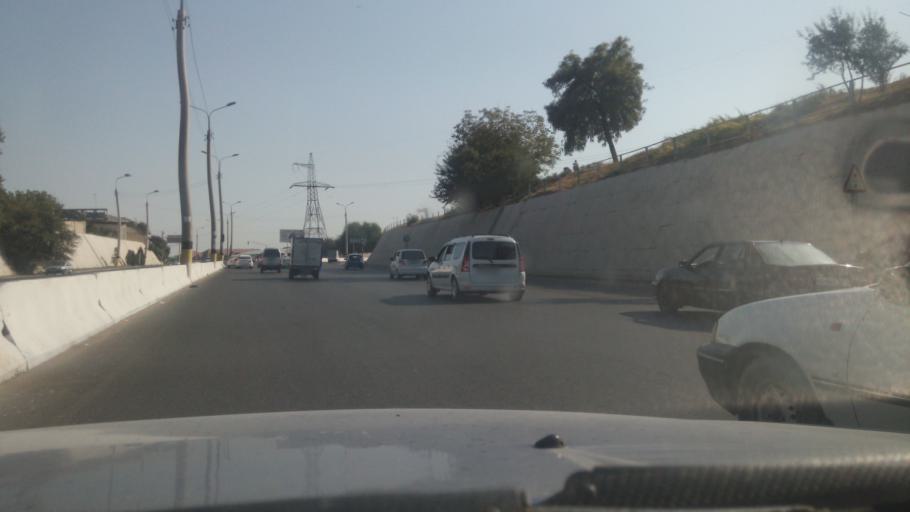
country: UZ
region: Toshkent Shahri
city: Tashkent
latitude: 41.2375
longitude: 69.1681
